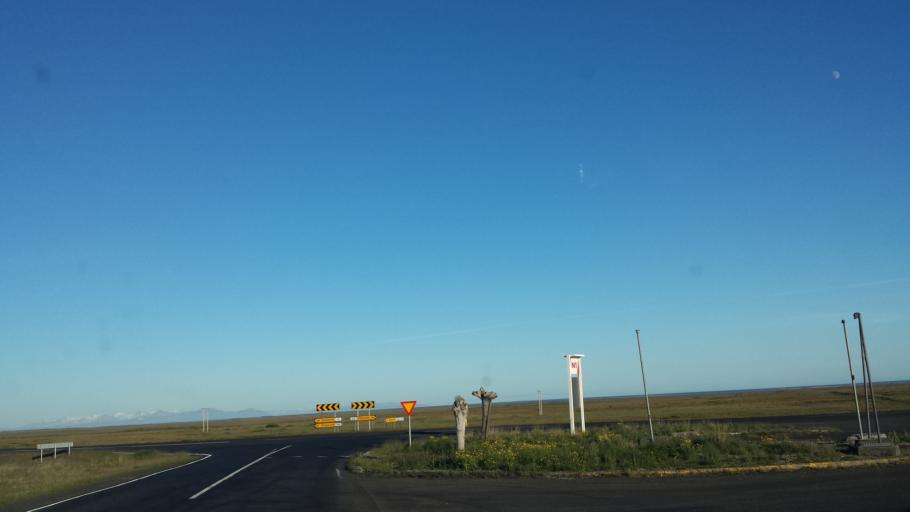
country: IS
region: West
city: Stykkisholmur
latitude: 64.8495
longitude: -22.7332
